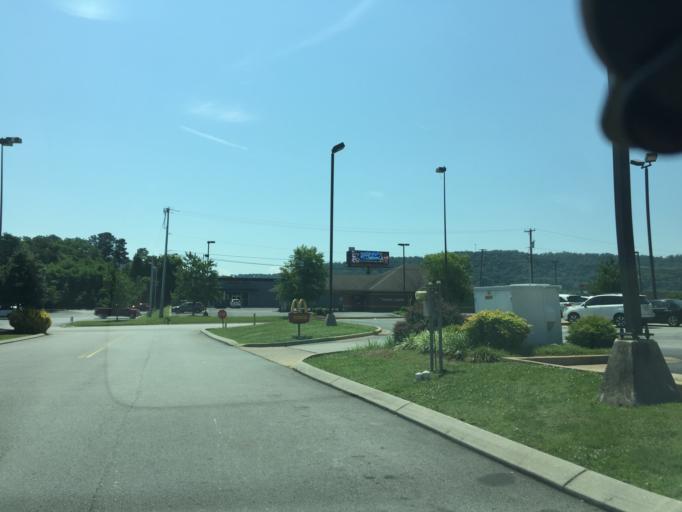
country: US
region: Tennessee
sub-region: Hamilton County
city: Collegedale
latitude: 35.0850
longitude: -85.0619
